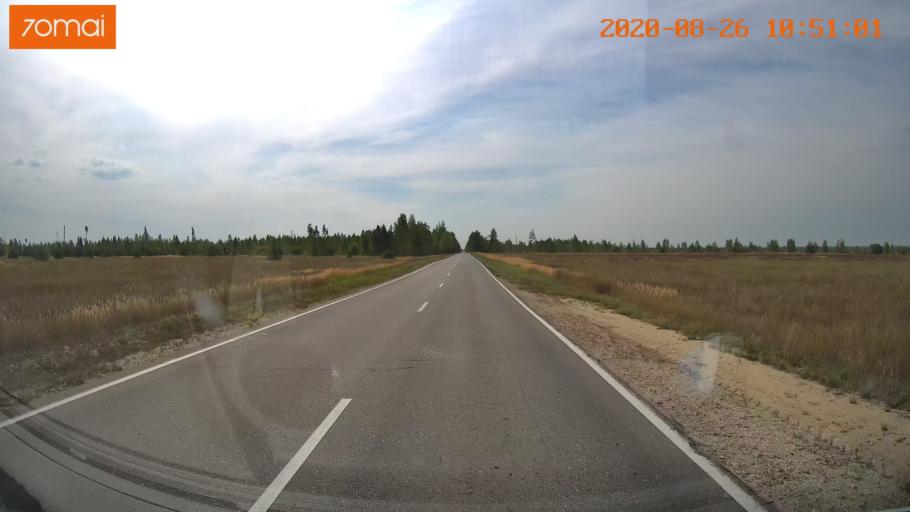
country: RU
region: Rjazan
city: Lashma
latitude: 54.6788
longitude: 41.1558
